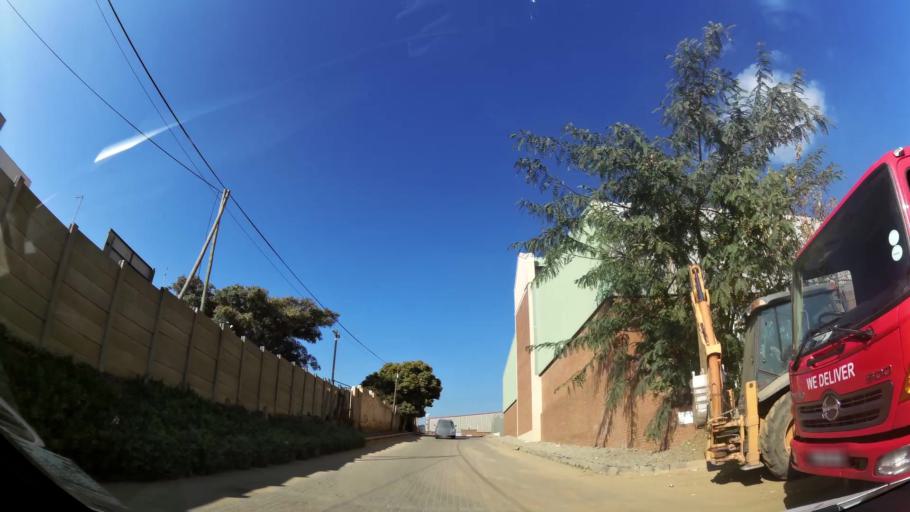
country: ZA
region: Gauteng
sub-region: Ekurhuleni Metropolitan Municipality
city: Germiston
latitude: -26.1674
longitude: 28.1600
